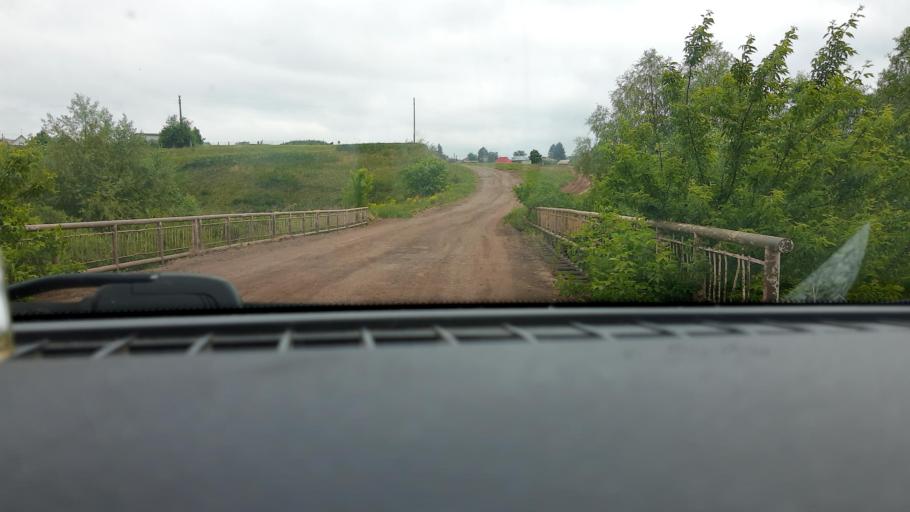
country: RU
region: Bashkortostan
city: Chishmy
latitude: 54.6820
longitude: 55.4814
